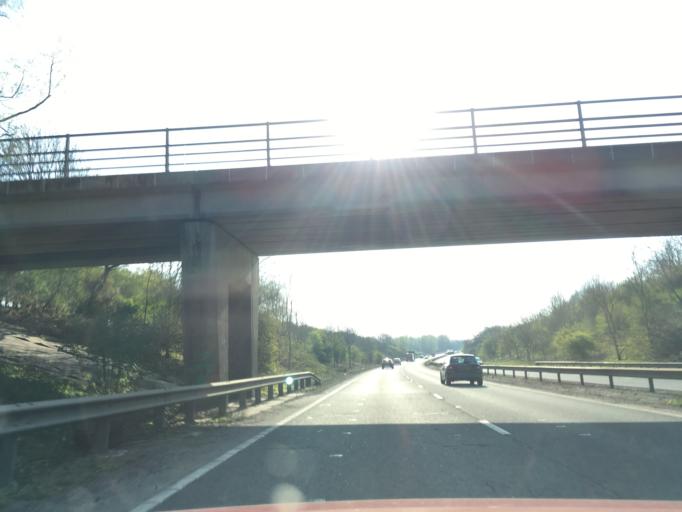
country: GB
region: England
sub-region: Milton Keynes
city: Stony Stratford
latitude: 52.0659
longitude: -0.8589
